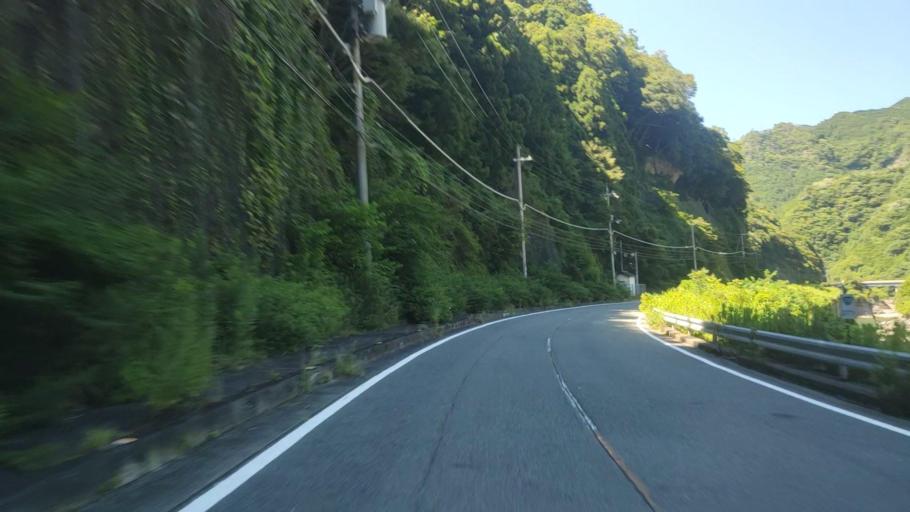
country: JP
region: Nara
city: Yoshino-cho
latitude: 34.3040
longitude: 135.9913
